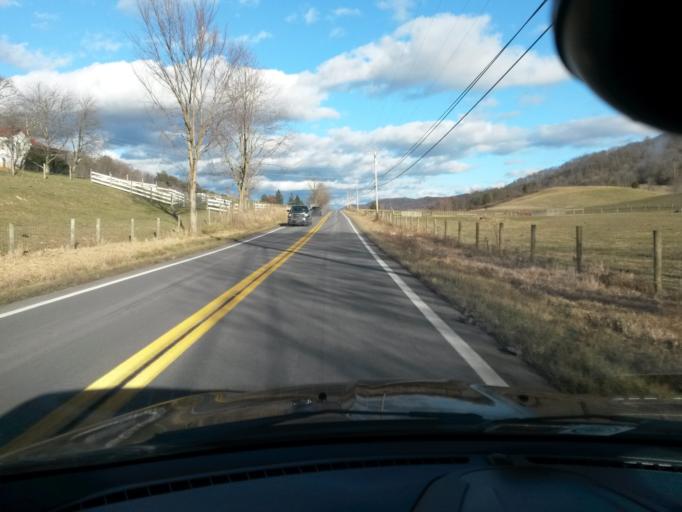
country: US
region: Virginia
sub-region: Giles County
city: Pearisburg
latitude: 37.4257
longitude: -80.7283
